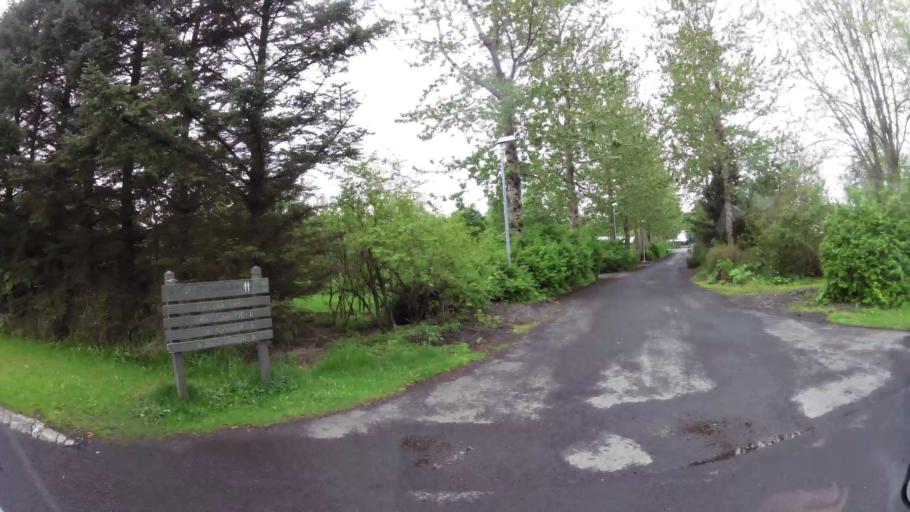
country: IS
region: Capital Region
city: Reykjavik
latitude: 64.1404
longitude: -21.8655
